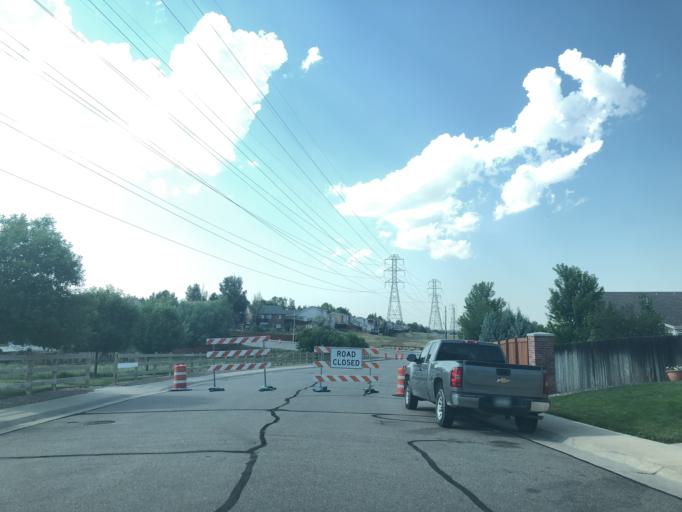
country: US
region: Colorado
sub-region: Arapahoe County
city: Dove Valley
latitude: 39.6371
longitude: -104.7538
